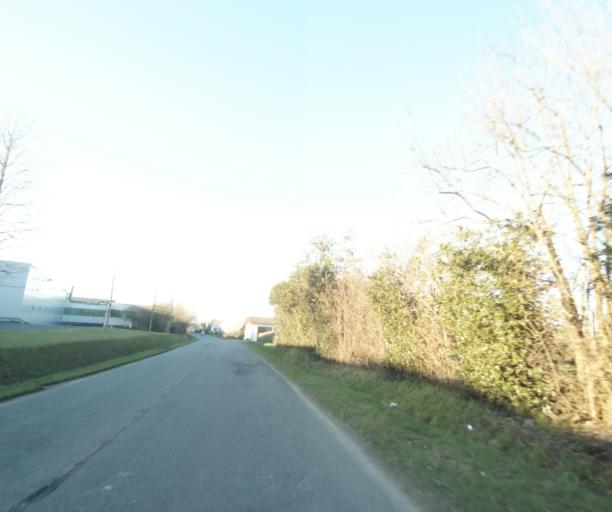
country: FR
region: Aquitaine
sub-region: Departement des Pyrenees-Atlantiques
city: Urrugne
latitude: 43.3504
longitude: -1.6887
